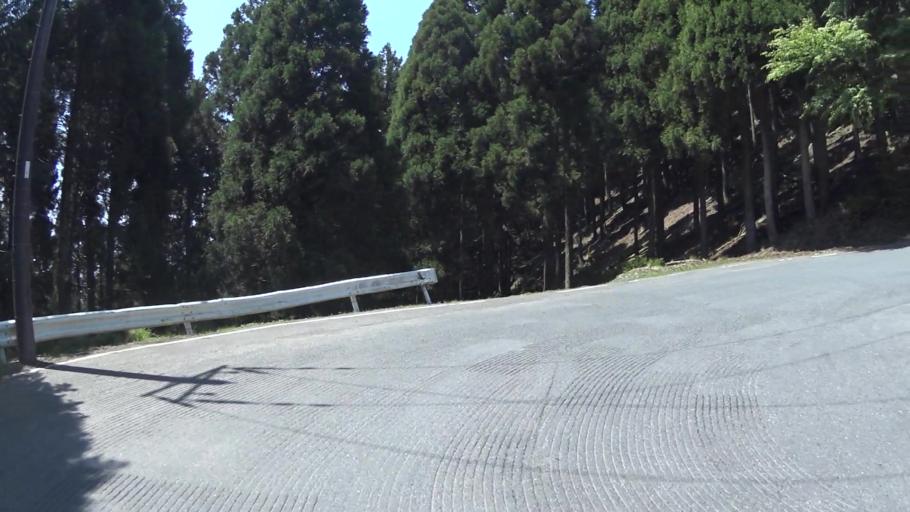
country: JP
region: Shiga Prefecture
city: Kitahama
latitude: 35.1553
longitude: 135.7883
